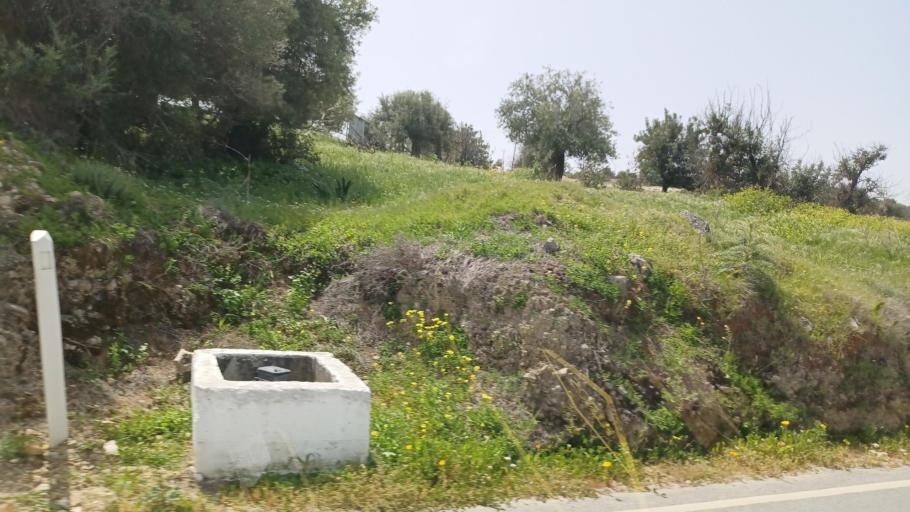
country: CY
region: Limassol
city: Pissouri
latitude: 34.6991
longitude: 32.7575
